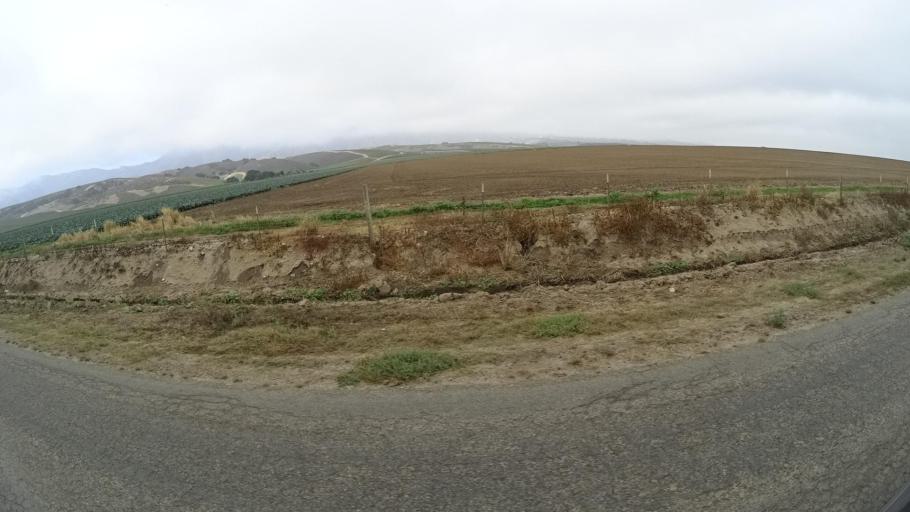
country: US
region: California
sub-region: Monterey County
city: Soledad
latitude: 36.3624
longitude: -121.3347
